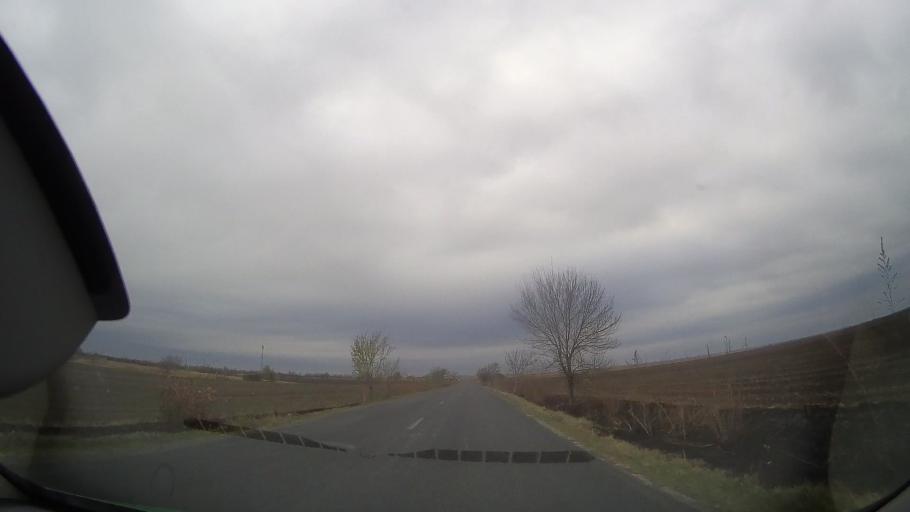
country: RO
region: Buzau
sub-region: Comuna Padina
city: Padina
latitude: 44.7827
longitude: 27.1505
